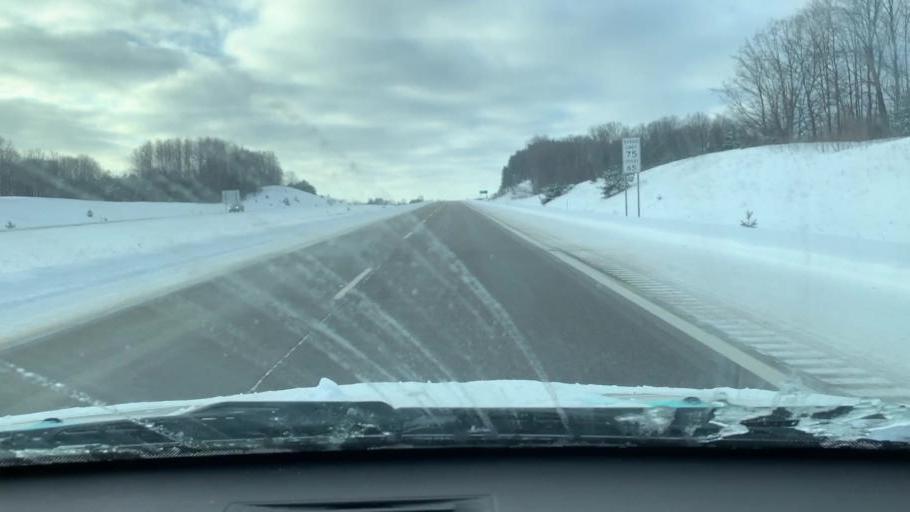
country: US
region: Michigan
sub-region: Wexford County
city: Manton
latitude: 44.3952
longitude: -85.3825
